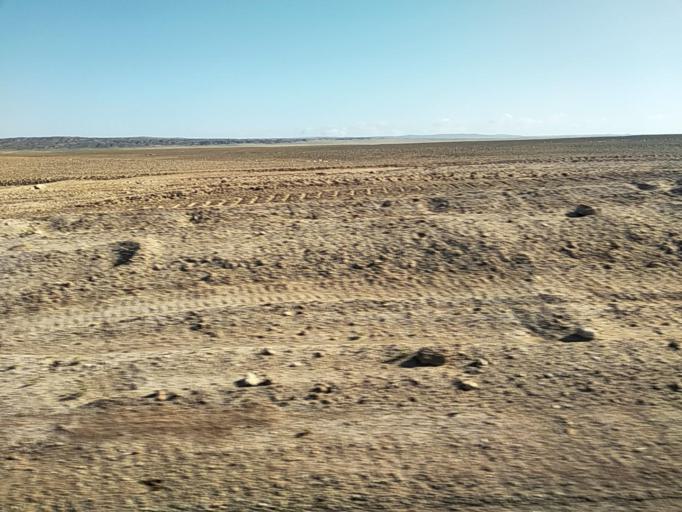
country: CL
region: Atacama
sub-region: Provincia de Copiapo
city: Copiapo
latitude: -27.3252
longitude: -70.8039
